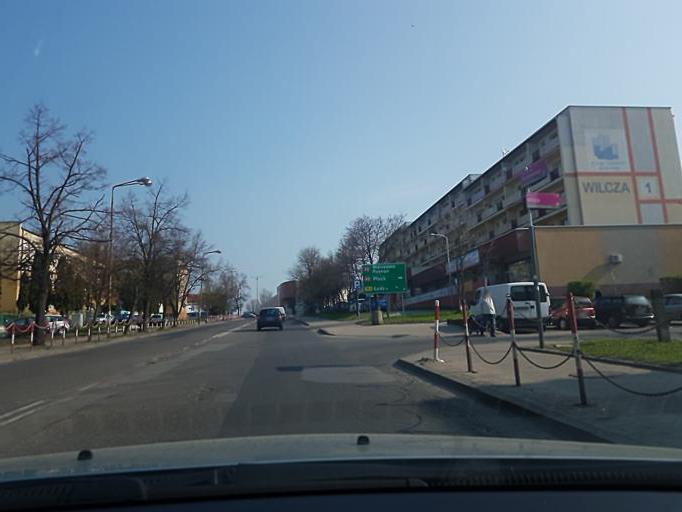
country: PL
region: Lodz Voivodeship
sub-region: Powiat kutnowski
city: Kutno
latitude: 52.2279
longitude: 19.3672
